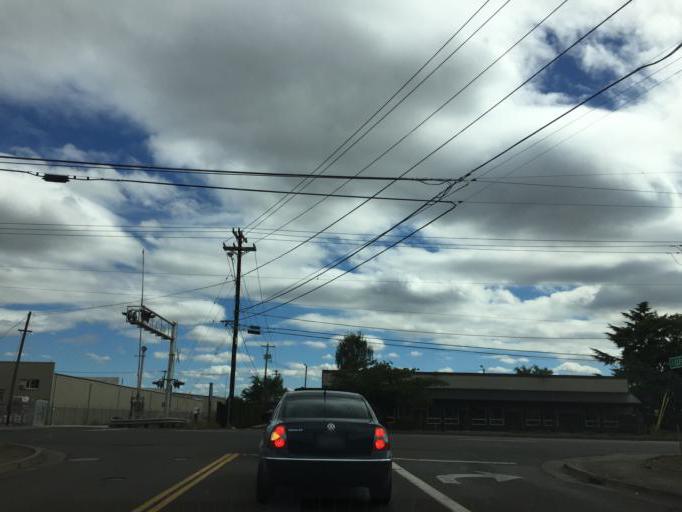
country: US
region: Oregon
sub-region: Marion County
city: Woodburn
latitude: 45.1359
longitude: -122.8454
